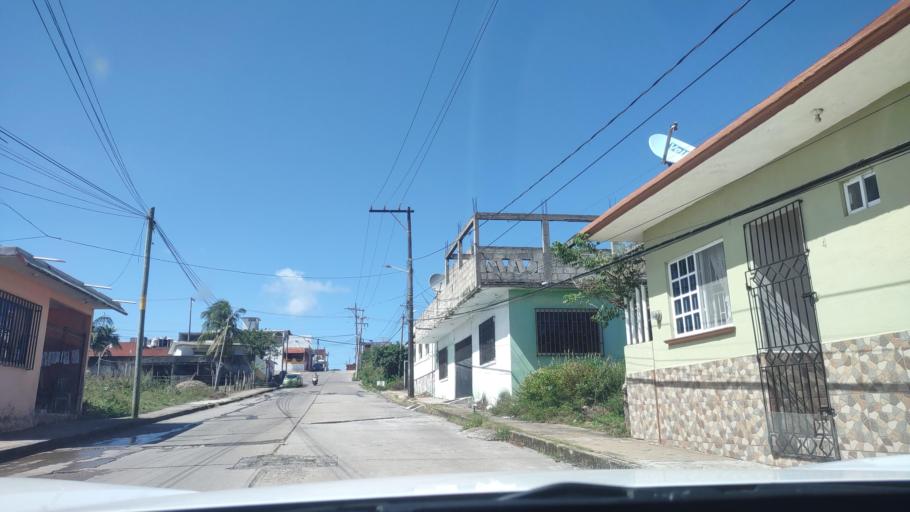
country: MX
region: Veracruz
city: Heroica Alvarado
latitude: 18.7831
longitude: -95.7713
